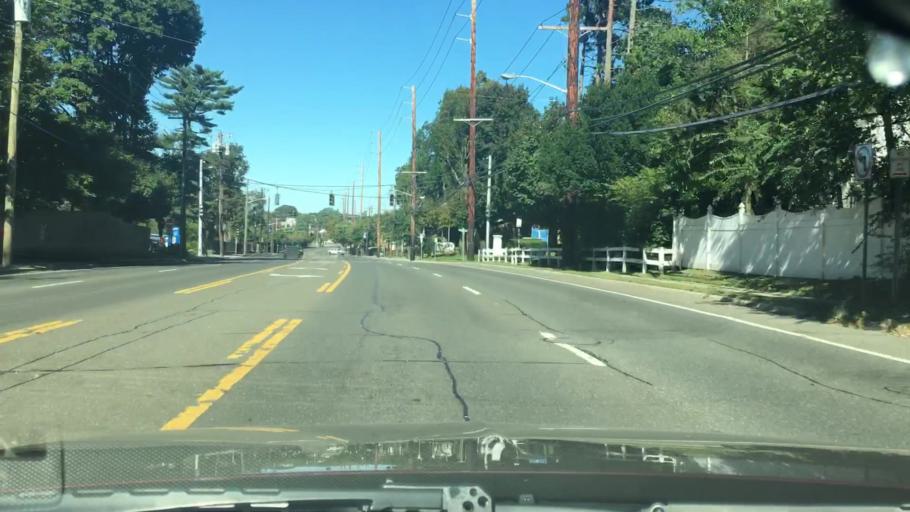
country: US
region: New York
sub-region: Nassau County
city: Flower Hill
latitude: 40.8210
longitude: -73.6806
